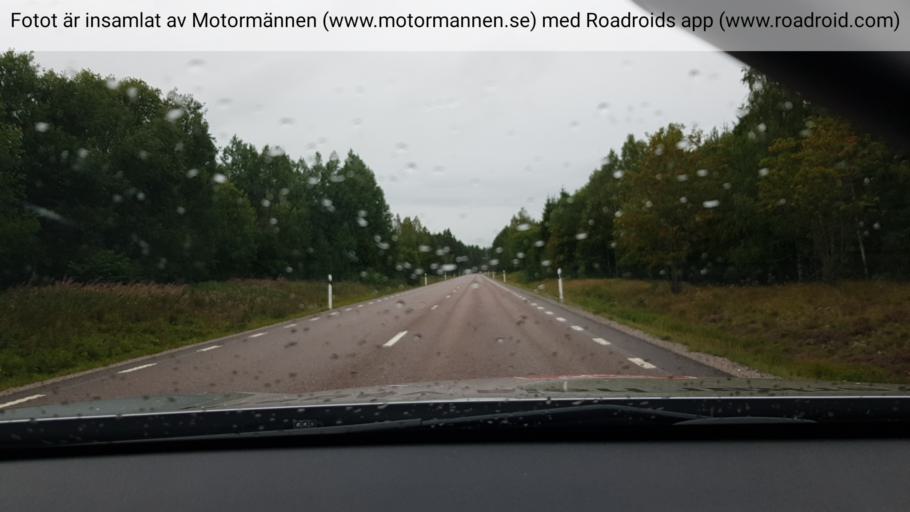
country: SE
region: Gaevleborg
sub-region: Gavle Kommun
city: Hedesunda
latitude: 60.4005
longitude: 16.9757
